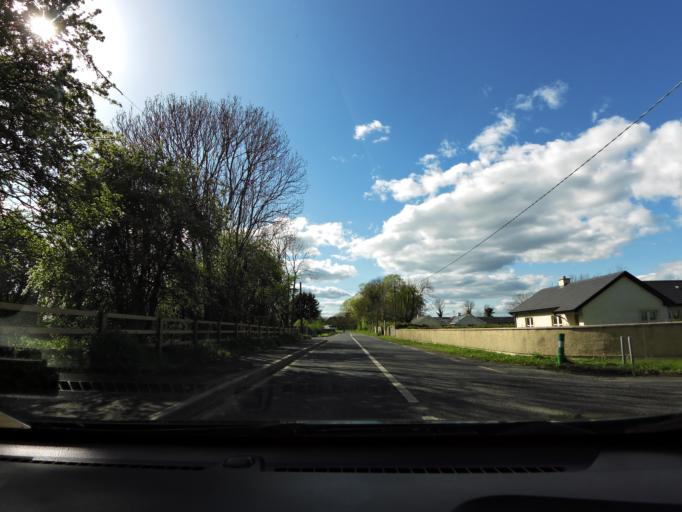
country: IE
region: Leinster
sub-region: Kildare
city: Maynooth
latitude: 53.3823
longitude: -6.6197
